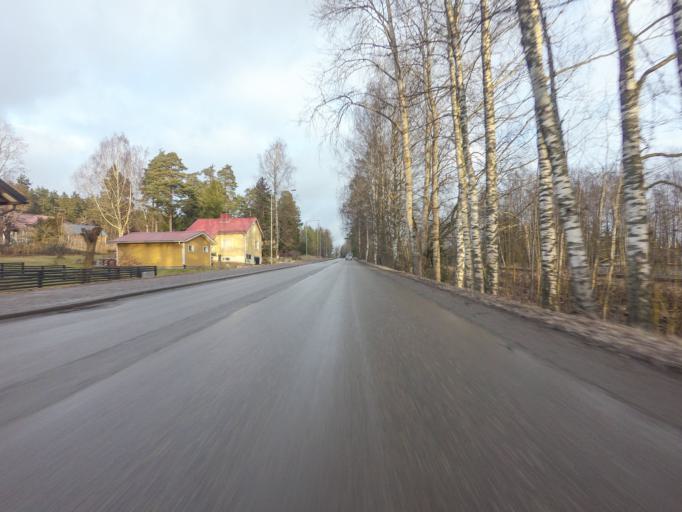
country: FI
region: Uusimaa
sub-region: Helsinki
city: Lohja
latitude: 60.2511
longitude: 24.0944
